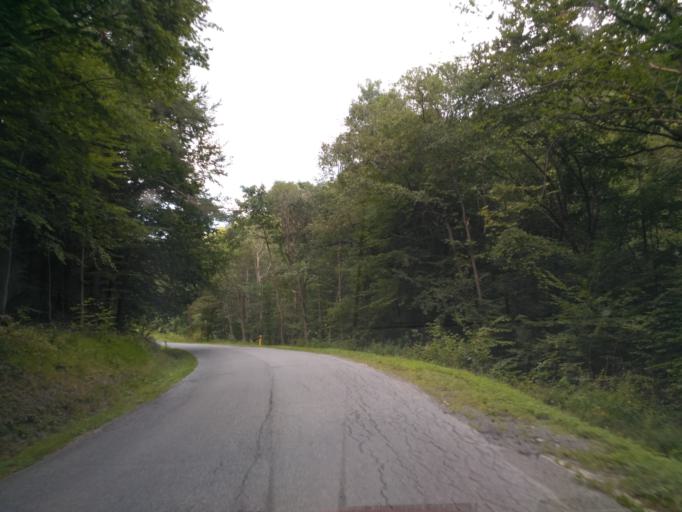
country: SK
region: Kosicky
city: Gelnica
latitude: 48.9213
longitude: 21.0391
